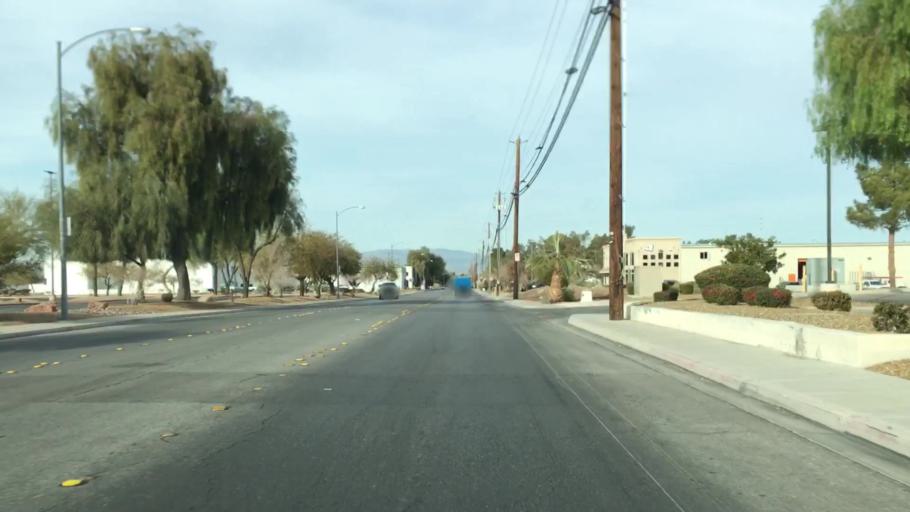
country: US
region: Nevada
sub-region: Clark County
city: Whitney
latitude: 36.0751
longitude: -115.0870
